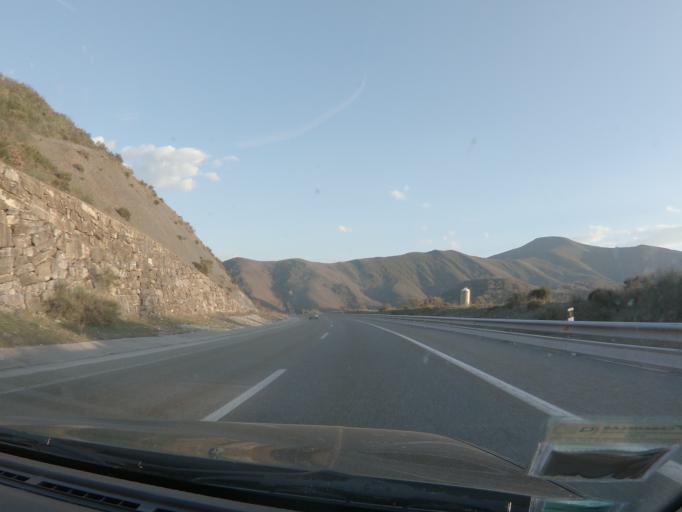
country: ES
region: Castille and Leon
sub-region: Provincia de Leon
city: Vega de Valcarce
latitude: 42.6783
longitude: -6.9888
